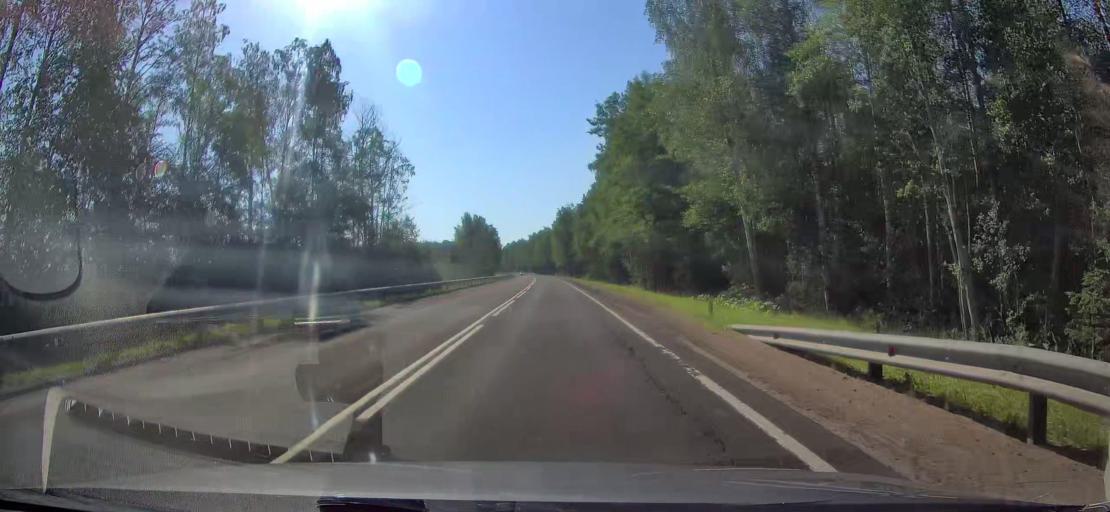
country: RU
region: Leningrad
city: Khvalovo
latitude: 59.8816
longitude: 32.8466
